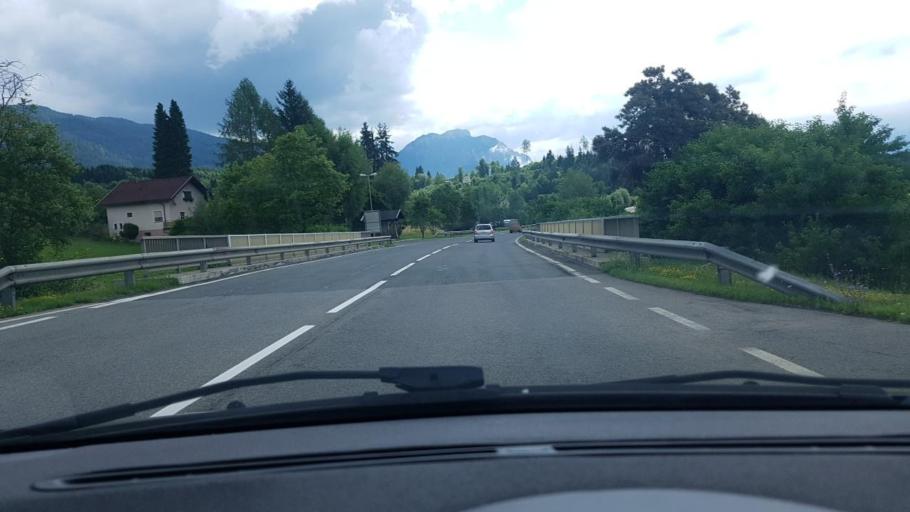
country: AT
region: Carinthia
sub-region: Politischer Bezirk Villach Land
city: Feistritz an der Gail
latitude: 46.6198
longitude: 13.5171
